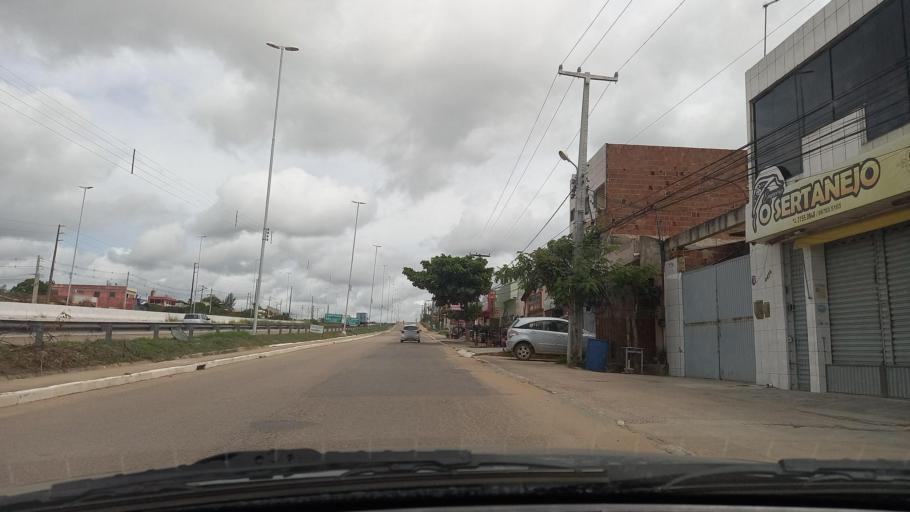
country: ET
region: Oromiya
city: Gore
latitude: 8.1969
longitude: 35.5788
